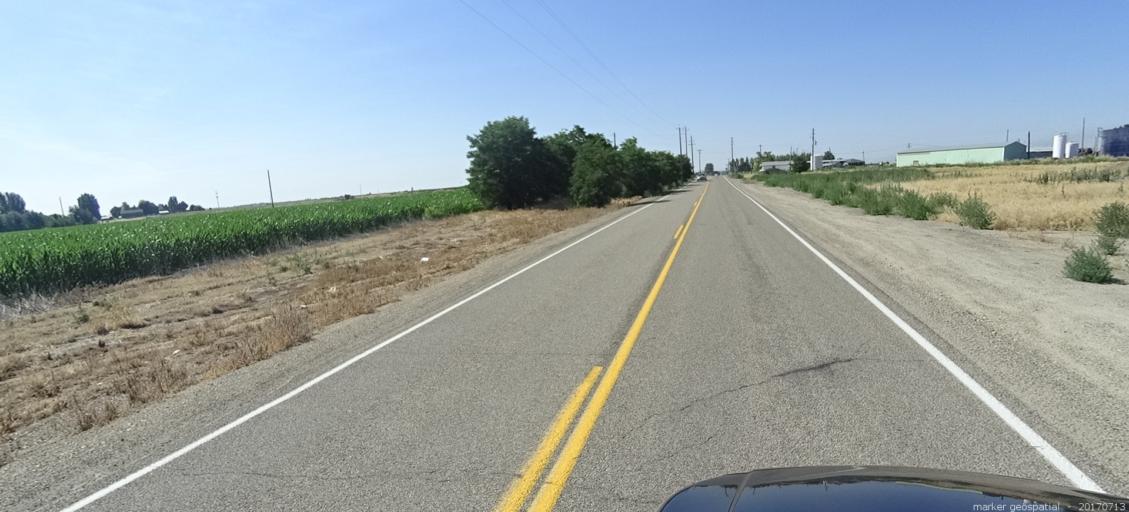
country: US
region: Idaho
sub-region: Ada County
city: Kuna
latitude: 43.5359
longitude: -116.3743
